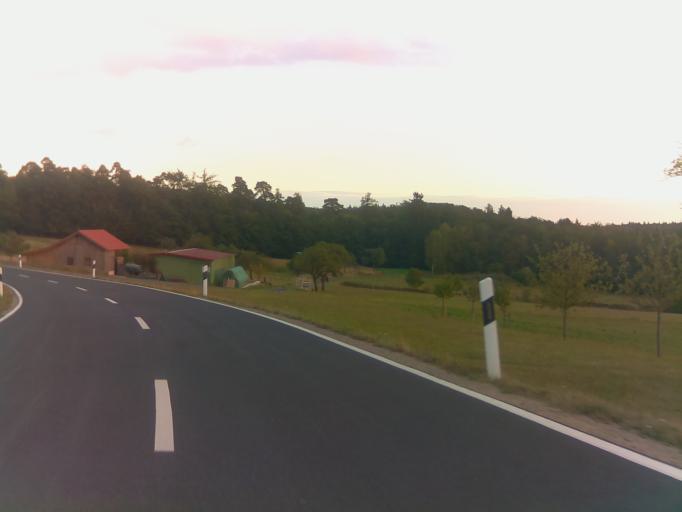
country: DE
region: Bavaria
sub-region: Regierungsbezirk Unterfranken
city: Schondra
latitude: 50.2505
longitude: 9.8883
